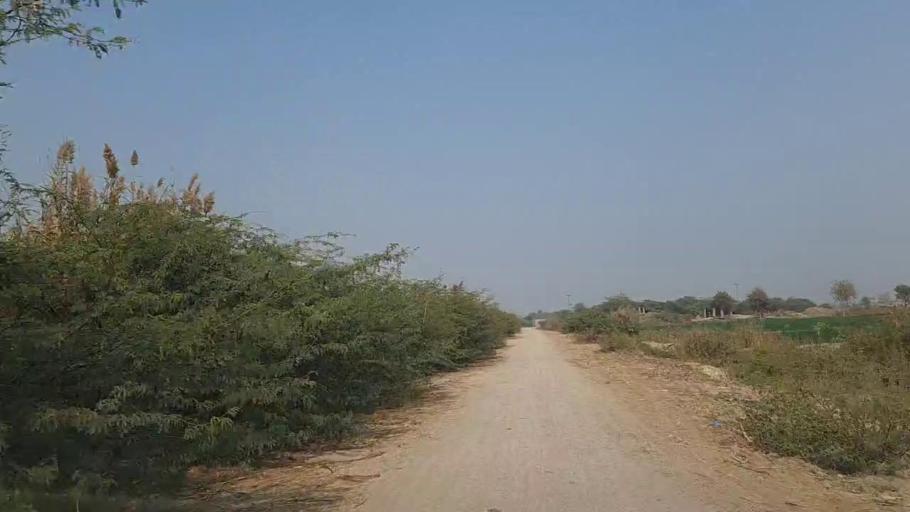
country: PK
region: Sindh
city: Daur
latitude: 26.4367
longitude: 68.4426
